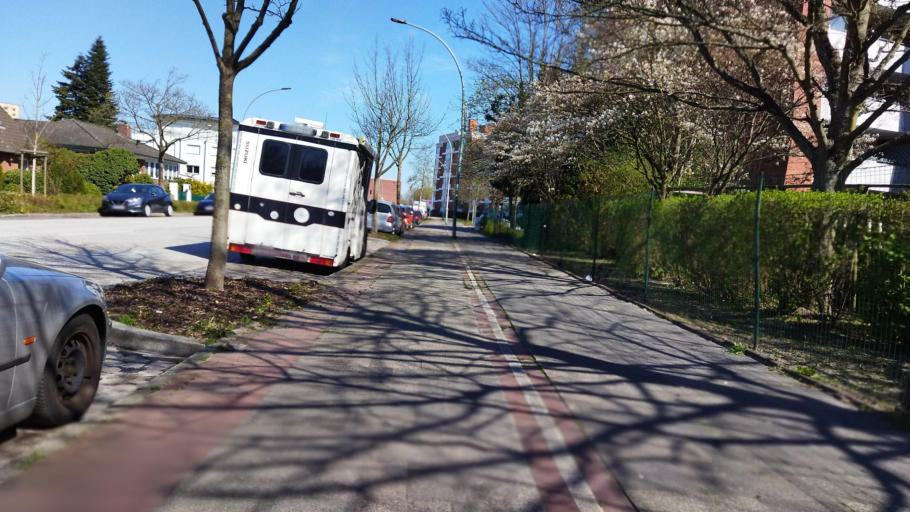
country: DE
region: Bremen
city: Bremerhaven
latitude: 53.5414
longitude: 8.5952
